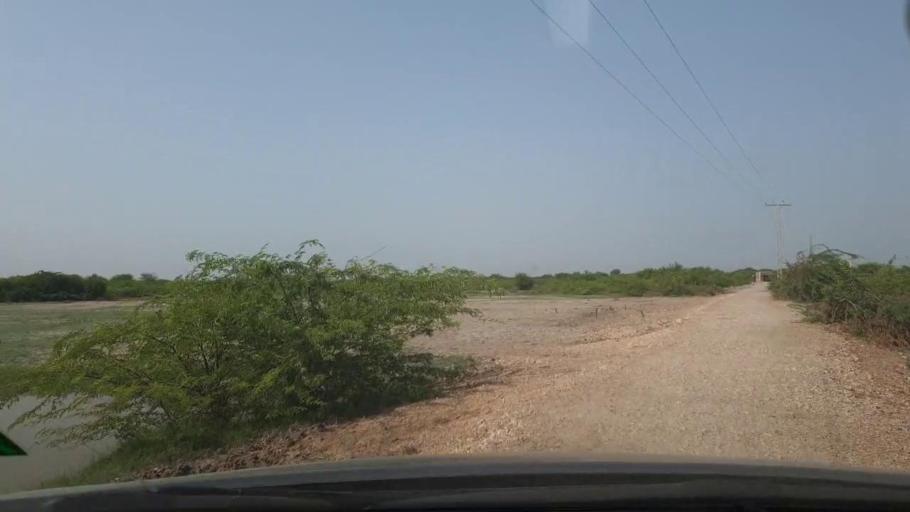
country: PK
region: Sindh
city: Naukot
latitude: 24.8018
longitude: 69.2401
